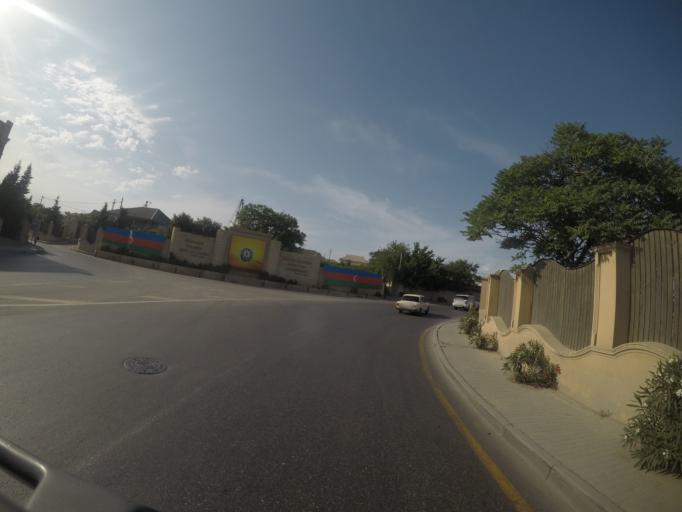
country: AZ
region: Baki
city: Binagadi
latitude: 40.4633
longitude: 49.8412
